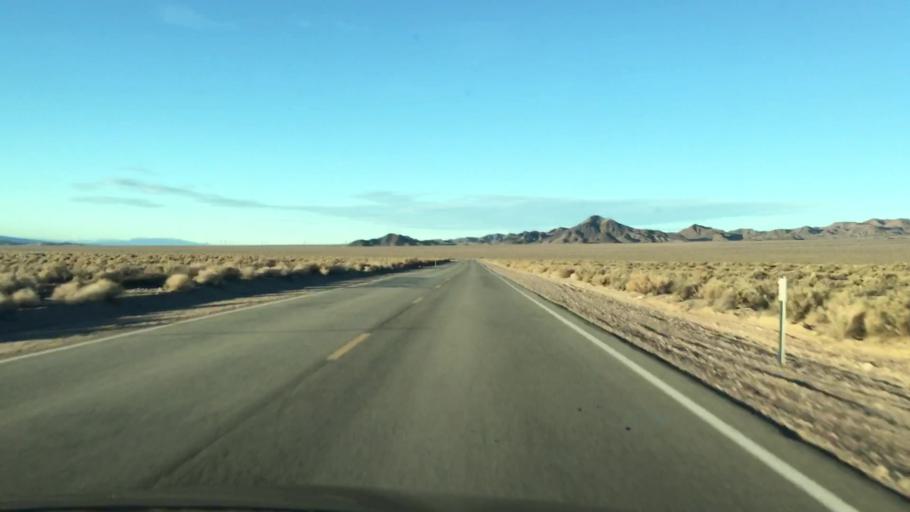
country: US
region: California
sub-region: San Bernardino County
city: Fort Irwin
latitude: 35.3330
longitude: -116.0816
